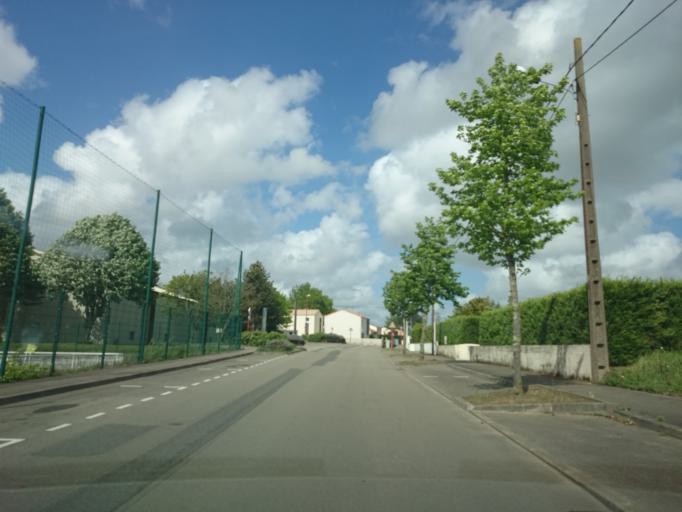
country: FR
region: Pays de la Loire
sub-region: Departement de la Loire-Atlantique
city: Bouaye
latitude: 47.1499
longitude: -1.6920
